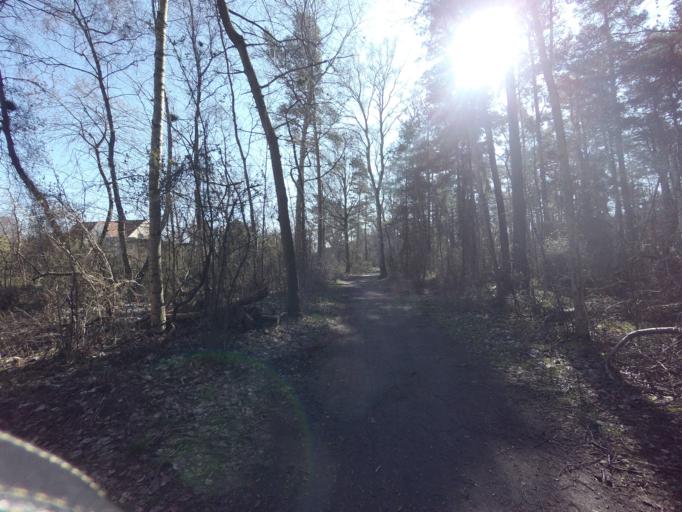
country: SE
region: Skane
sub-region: Vellinge Kommun
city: Skanor med Falsterbo
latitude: 55.4094
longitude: 12.8499
